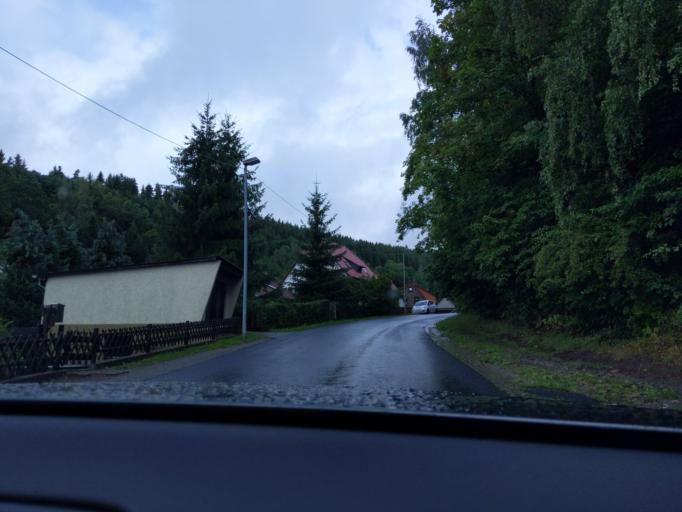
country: DE
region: Thuringia
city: Suhl
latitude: 50.6022
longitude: 10.6565
